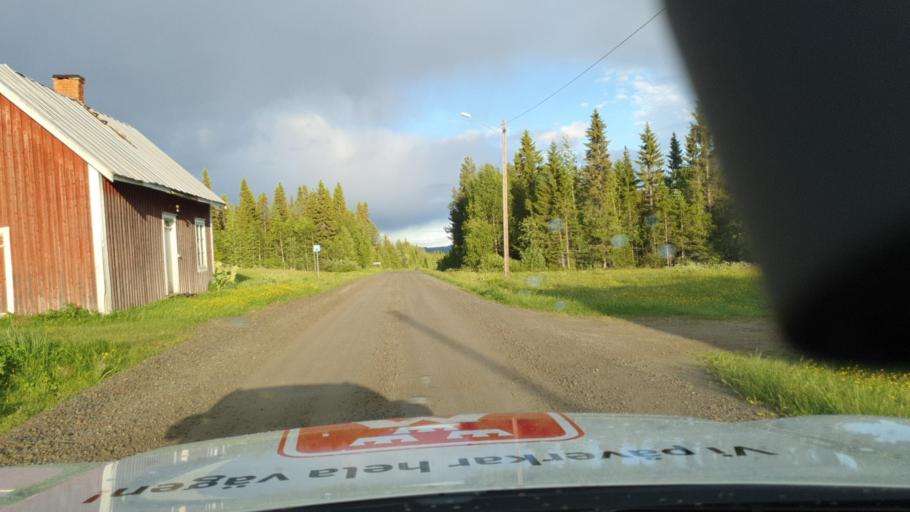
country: SE
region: Vaesterbotten
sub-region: Storumans Kommun
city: Storuman
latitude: 64.7612
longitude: 17.0674
